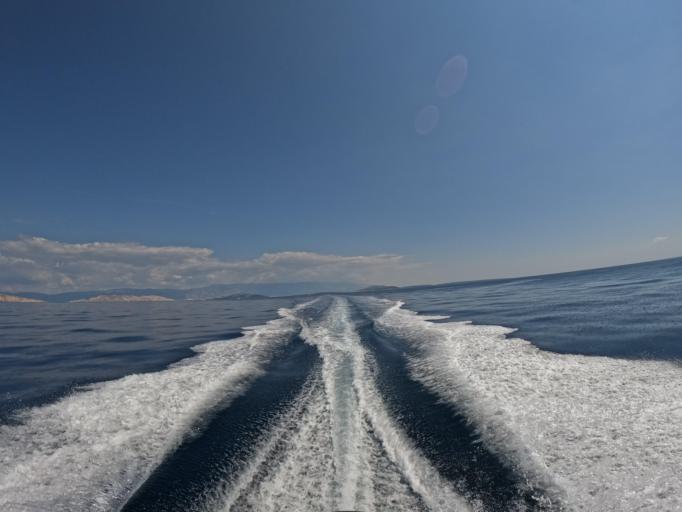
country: HR
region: Primorsko-Goranska
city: Punat
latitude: 44.9089
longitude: 14.5954
